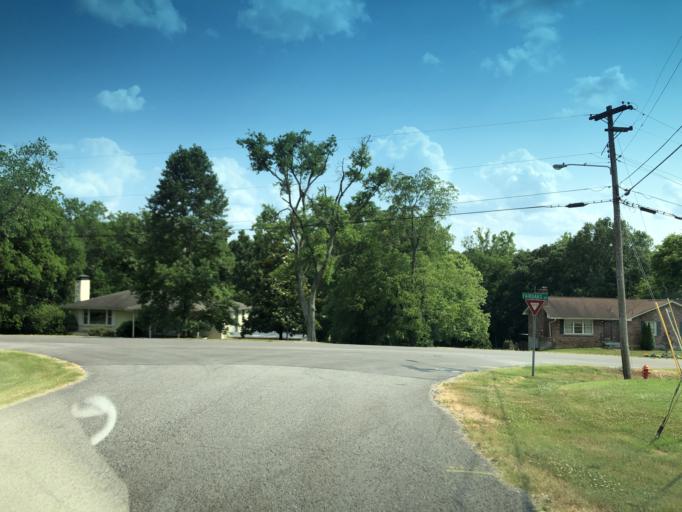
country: US
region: Tennessee
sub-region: Davidson County
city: Goodlettsville
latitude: 36.2521
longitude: -86.7318
